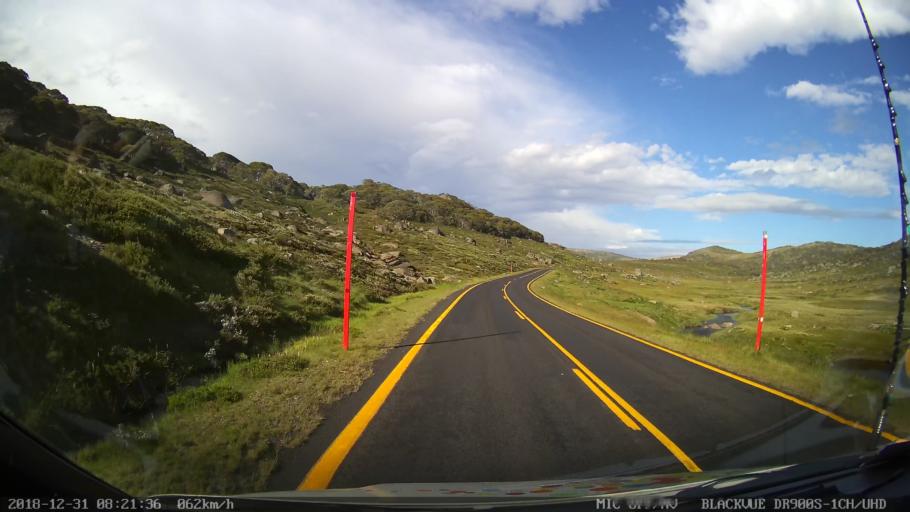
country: AU
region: New South Wales
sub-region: Snowy River
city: Jindabyne
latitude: -36.4278
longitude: 148.3668
